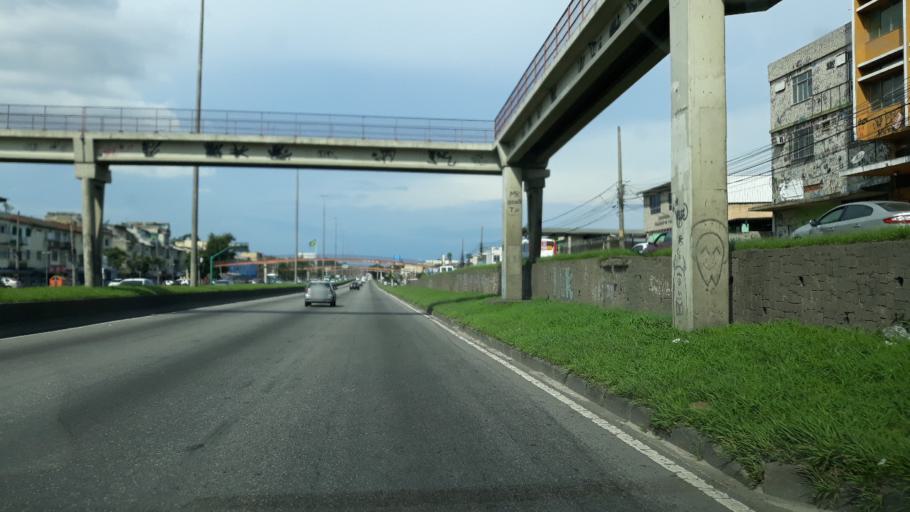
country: BR
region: Rio de Janeiro
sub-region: Sao Joao De Meriti
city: Sao Joao de Meriti
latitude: -22.8467
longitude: -43.3798
